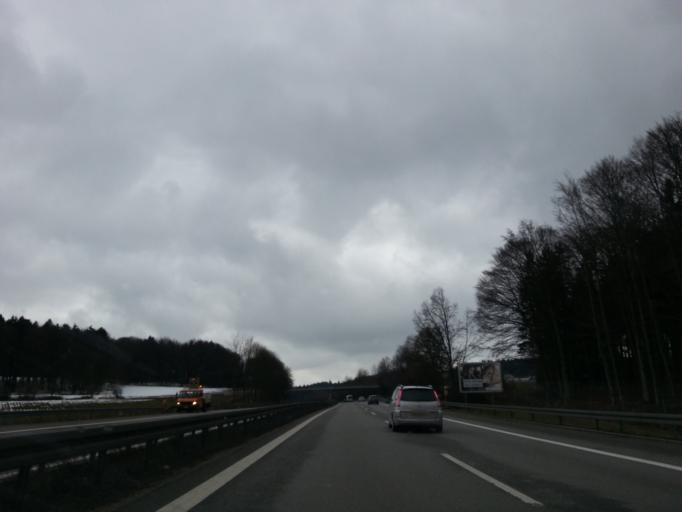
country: DE
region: Bavaria
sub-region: Upper Palatinate
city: Hohenfels
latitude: 49.1704
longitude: 11.8102
